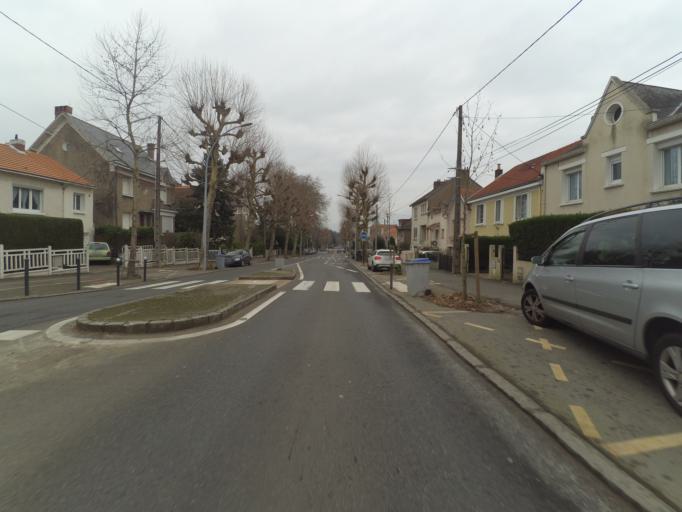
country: FR
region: Pays de la Loire
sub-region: Departement de la Loire-Atlantique
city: Nantes
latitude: 47.2219
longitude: -1.5891
